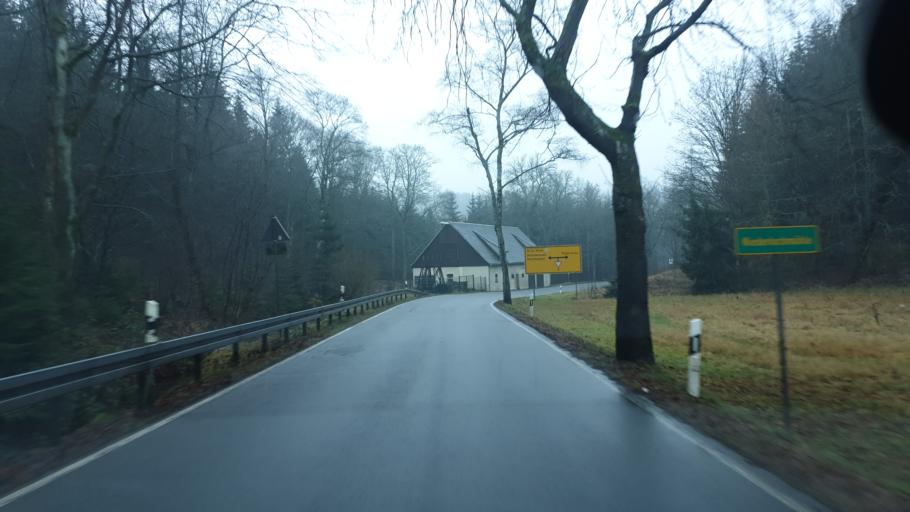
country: DE
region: Saxony
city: Seiffen
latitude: 50.6279
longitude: 13.4127
